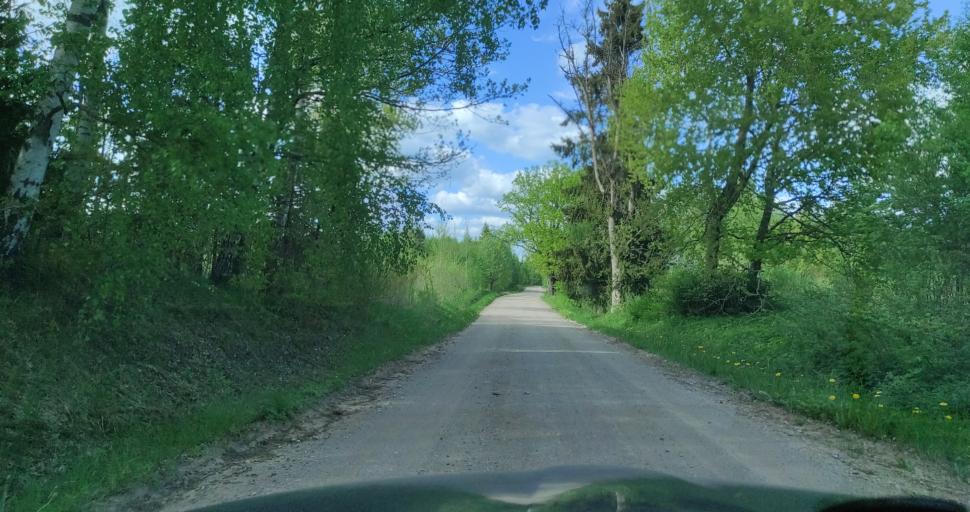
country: LV
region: Kuldigas Rajons
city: Kuldiga
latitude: 56.9472
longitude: 21.9114
